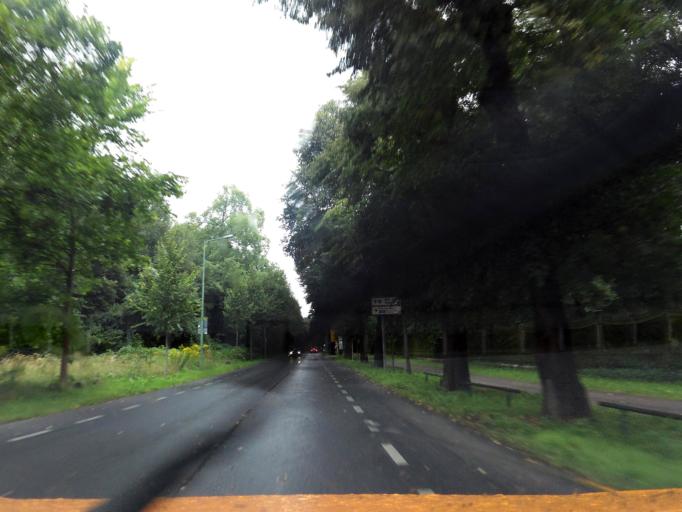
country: DE
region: Brandenburg
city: Potsdam
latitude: 52.4044
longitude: 13.0141
